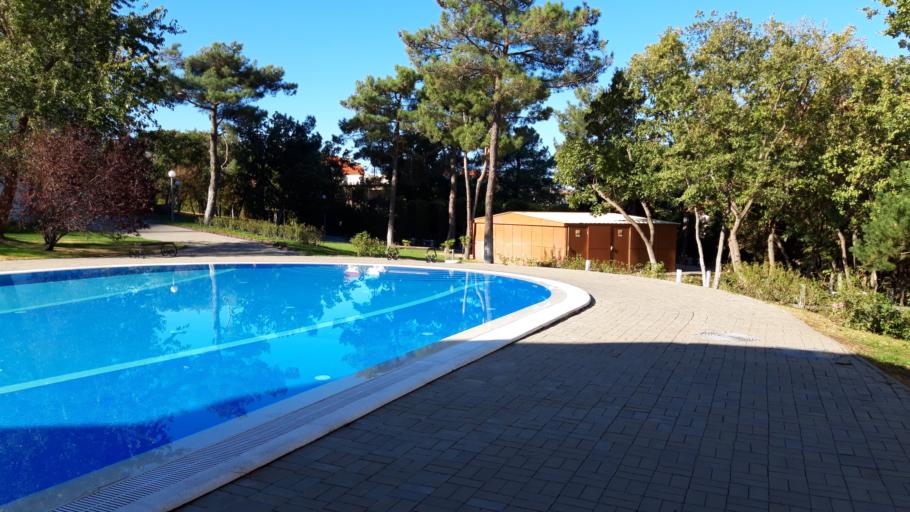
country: RU
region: Krasnodarskiy
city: Gelendzhik
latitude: 44.5521
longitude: 38.0543
